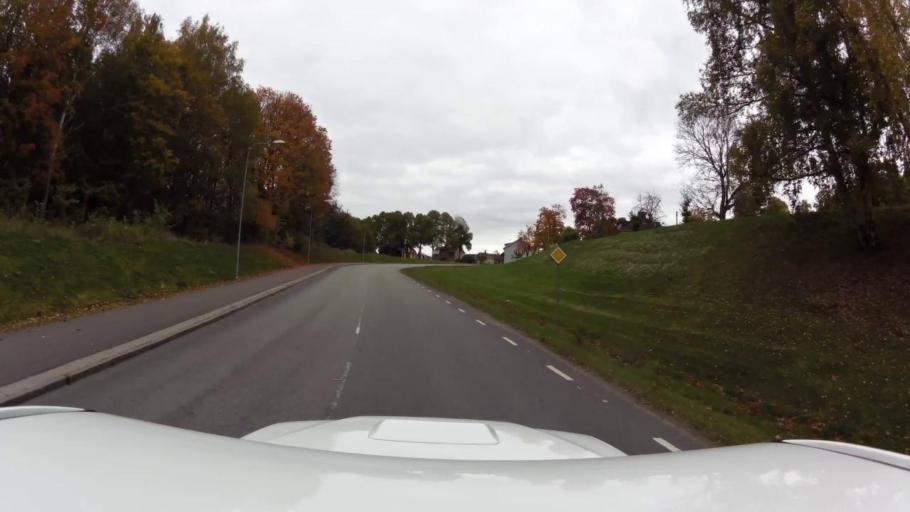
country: SE
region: OEstergoetland
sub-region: Linkopings Kommun
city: Ljungsbro
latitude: 58.5127
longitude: 15.5021
